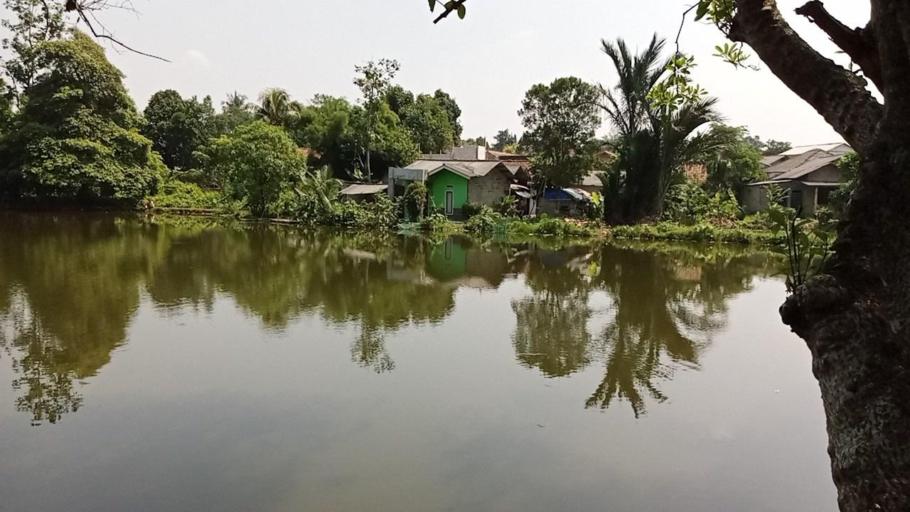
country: ID
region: West Java
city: Parung
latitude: -6.4234
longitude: 106.7488
